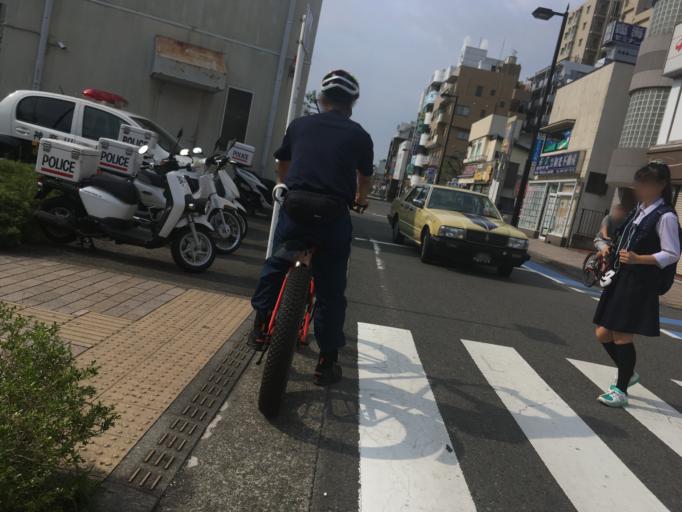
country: JP
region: Kanagawa
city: Minami-rinkan
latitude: 35.4706
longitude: 139.4607
